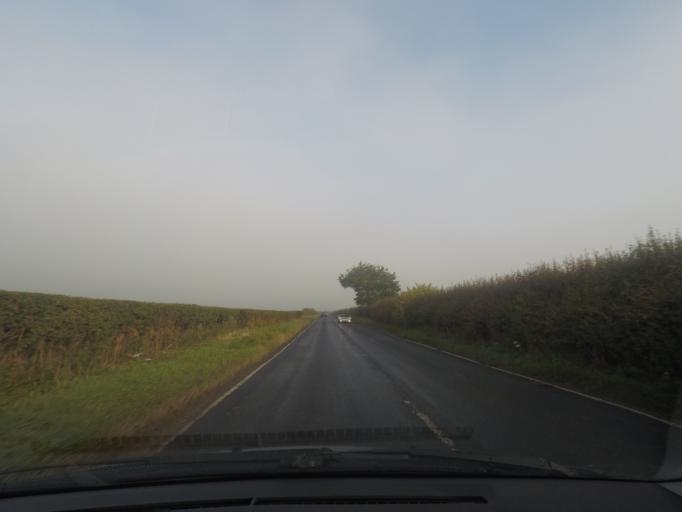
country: GB
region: England
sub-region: City and Borough of Leeds
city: Walton
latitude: 54.0088
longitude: -1.3070
